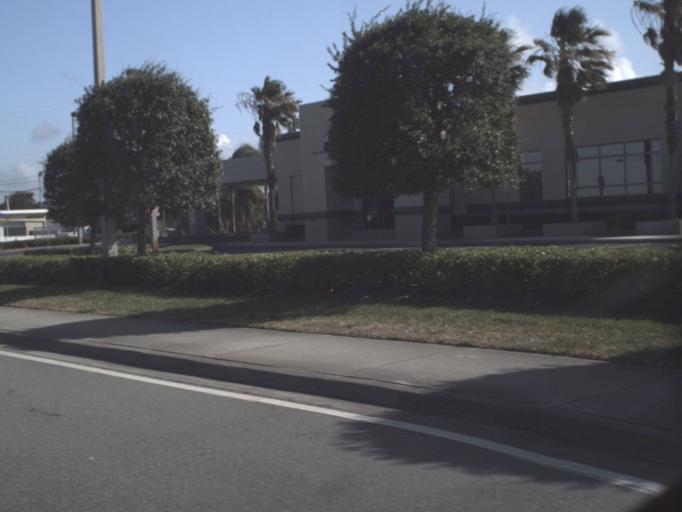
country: US
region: Florida
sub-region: Brevard County
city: Melbourne
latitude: 28.1132
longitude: -80.6197
